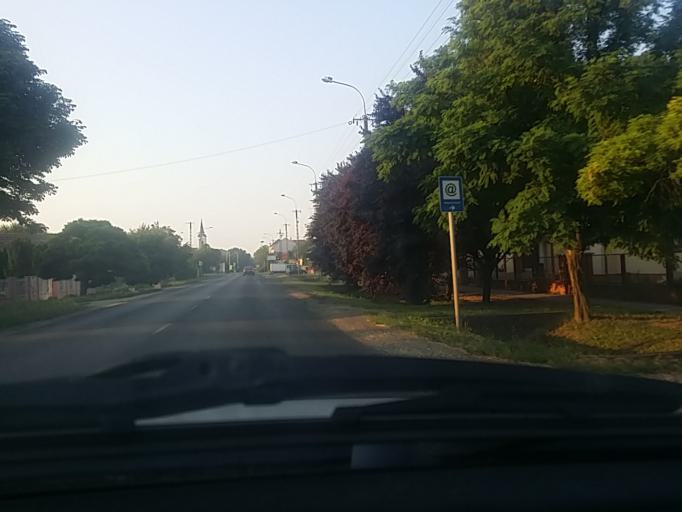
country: HU
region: Pest
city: Nagykata
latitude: 47.4217
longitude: 19.7400
